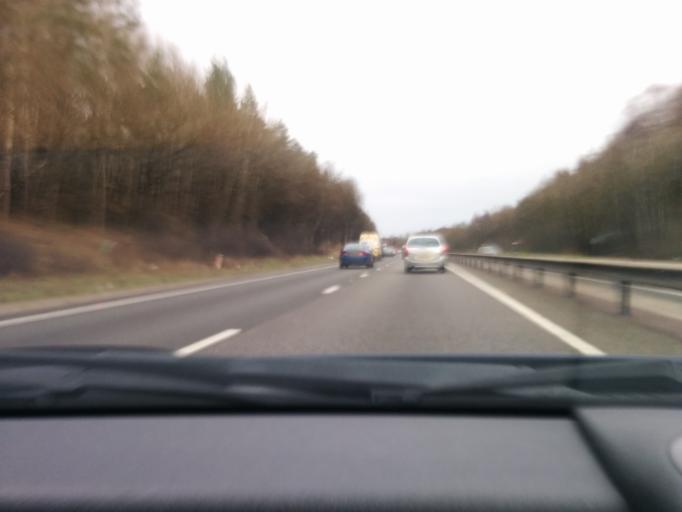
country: GB
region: England
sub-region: Oxfordshire
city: Radley
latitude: 51.7096
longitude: -1.2561
